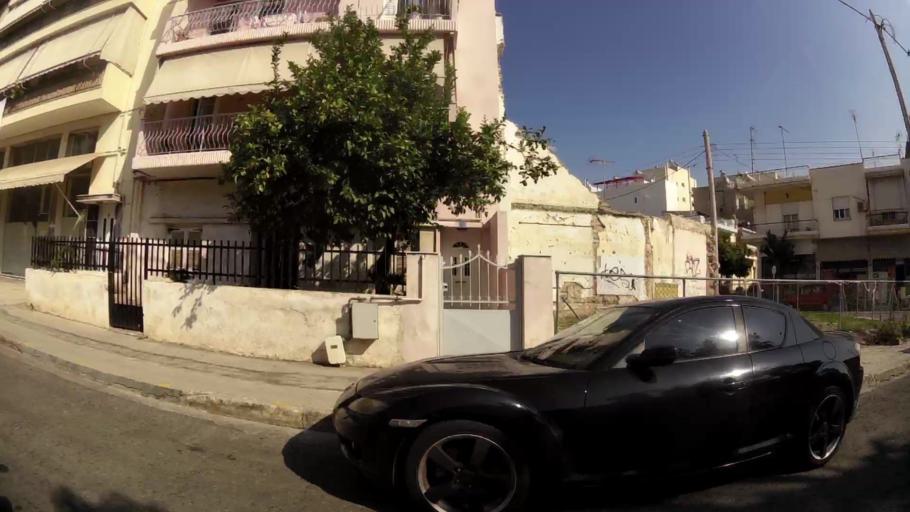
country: GR
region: Attica
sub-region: Nomos Piraios
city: Drapetsona
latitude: 37.9526
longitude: 23.6166
